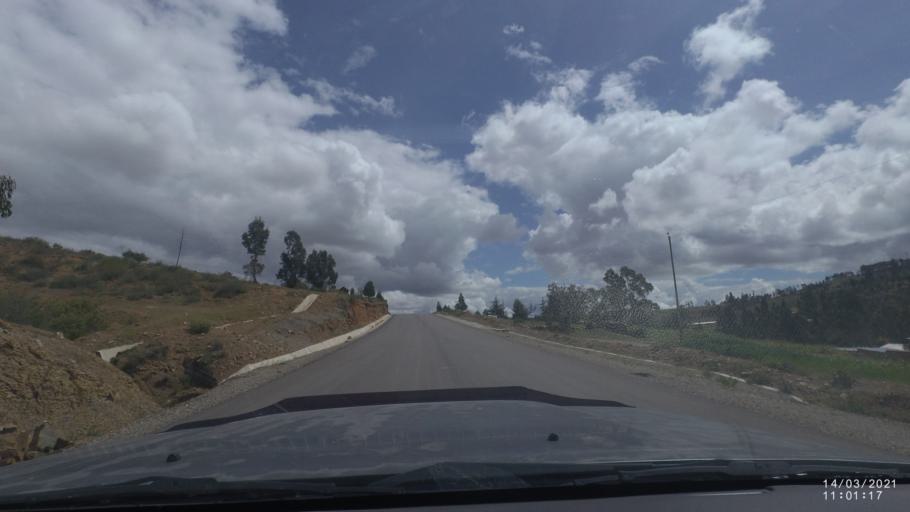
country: BO
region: Cochabamba
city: Tarata
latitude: -17.7964
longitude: -65.9633
